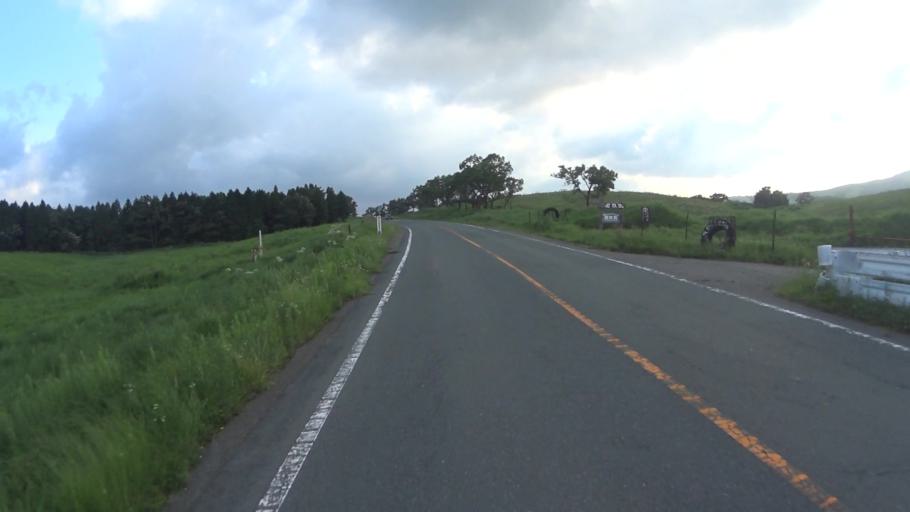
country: JP
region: Kumamoto
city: Aso
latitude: 33.0088
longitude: 131.0272
